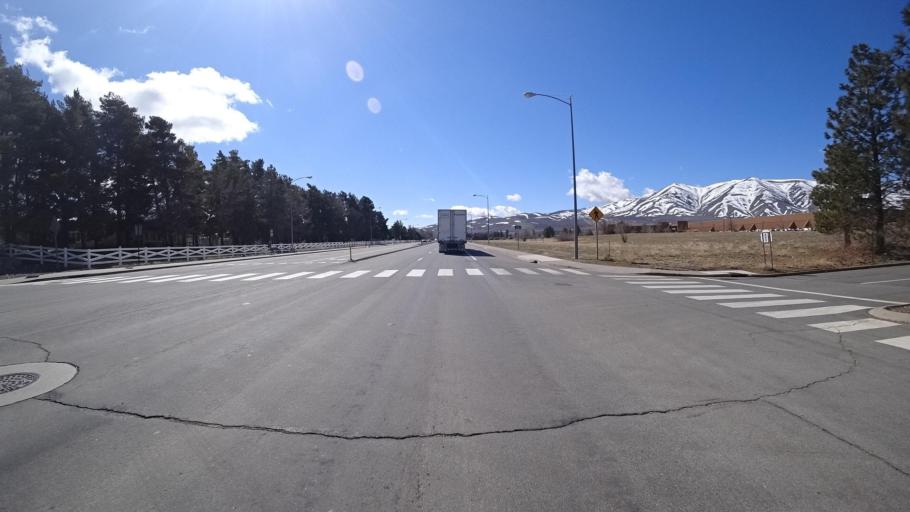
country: US
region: Nevada
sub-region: Washoe County
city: Lemmon Valley
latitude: 39.6401
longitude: -119.8819
